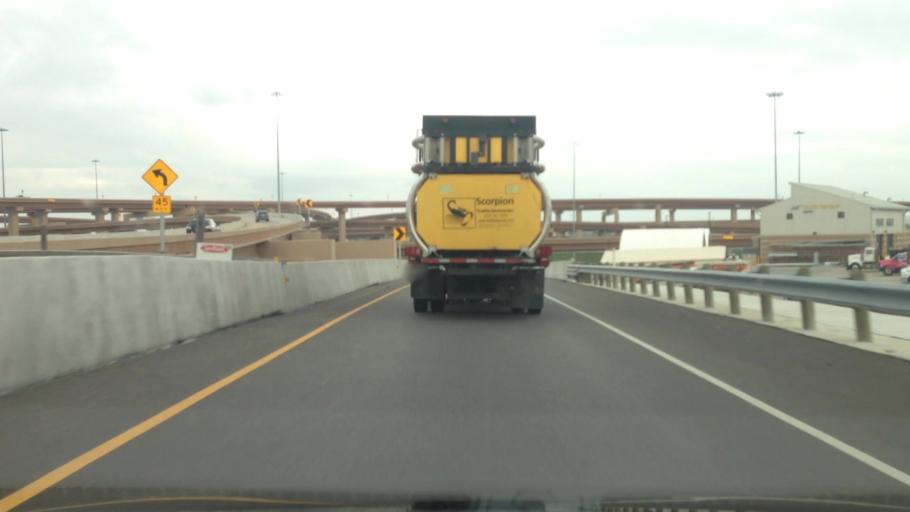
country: US
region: Texas
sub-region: Tarrant County
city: Blue Mound
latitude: 32.8391
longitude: -97.3164
